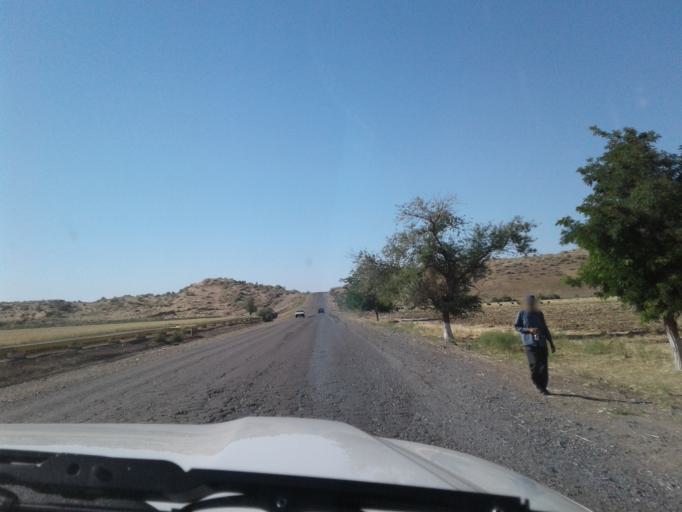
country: TM
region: Mary
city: Yoloeten
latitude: 36.7013
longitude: 62.4576
